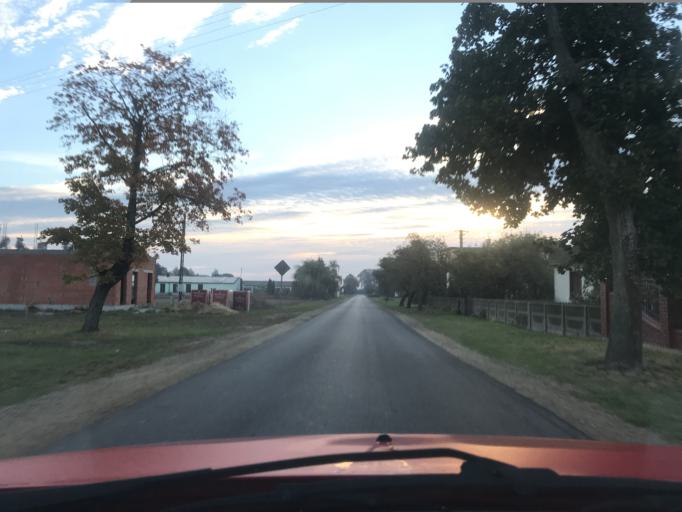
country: PL
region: Greater Poland Voivodeship
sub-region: Powiat ostrowski
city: Raszkow
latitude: 51.7194
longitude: 17.7855
